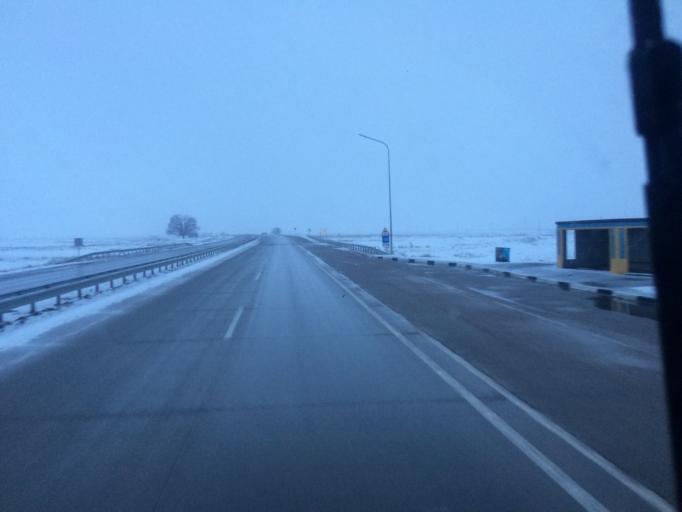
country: KZ
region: Zhambyl
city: Kulan
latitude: 42.9729
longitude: 72.4096
